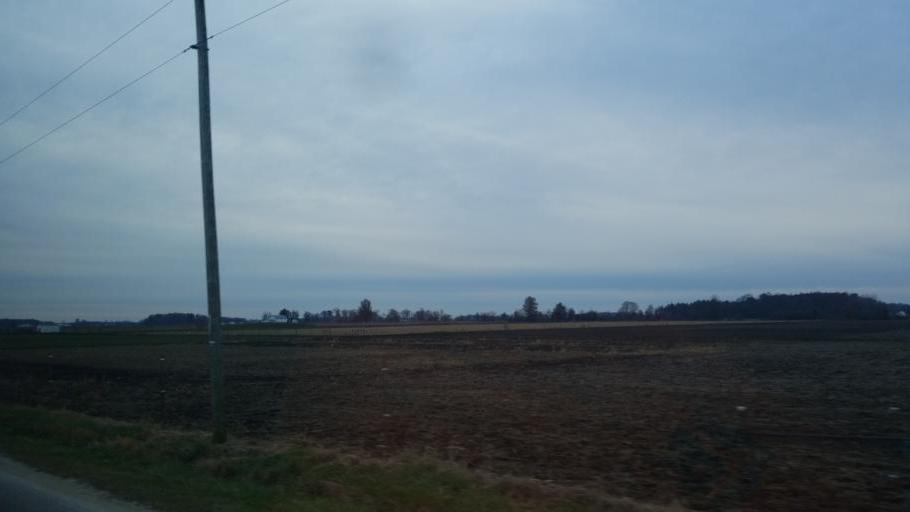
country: US
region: Indiana
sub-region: Adams County
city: Berne
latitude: 40.7122
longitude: -84.8791
